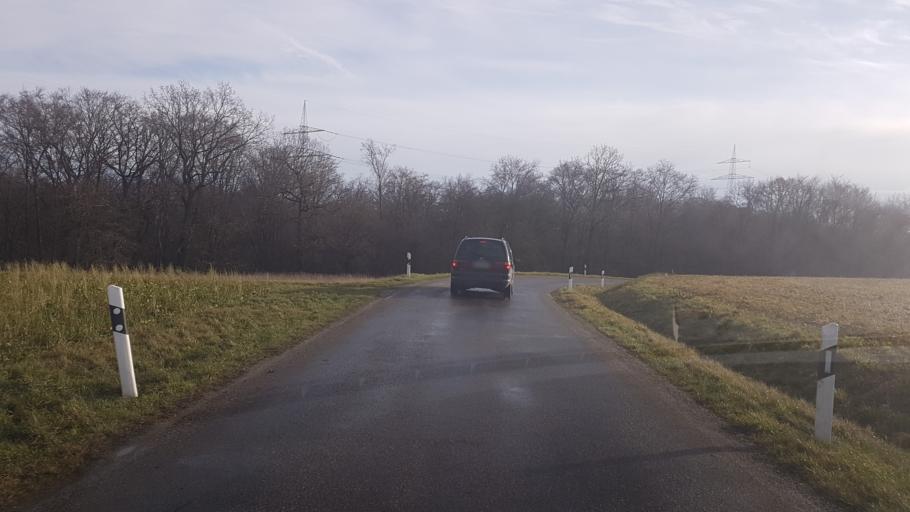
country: DE
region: Baden-Wuerttemberg
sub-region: Regierungsbezirk Stuttgart
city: Braunsbach
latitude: 49.2029
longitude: 9.7464
